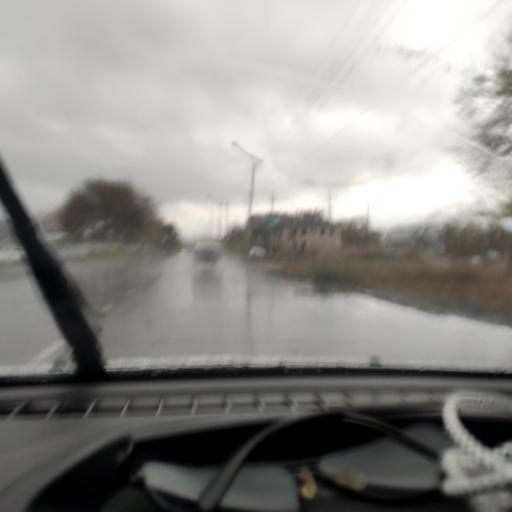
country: RU
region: Samara
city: Zhigulevsk
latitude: 53.4746
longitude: 49.5337
